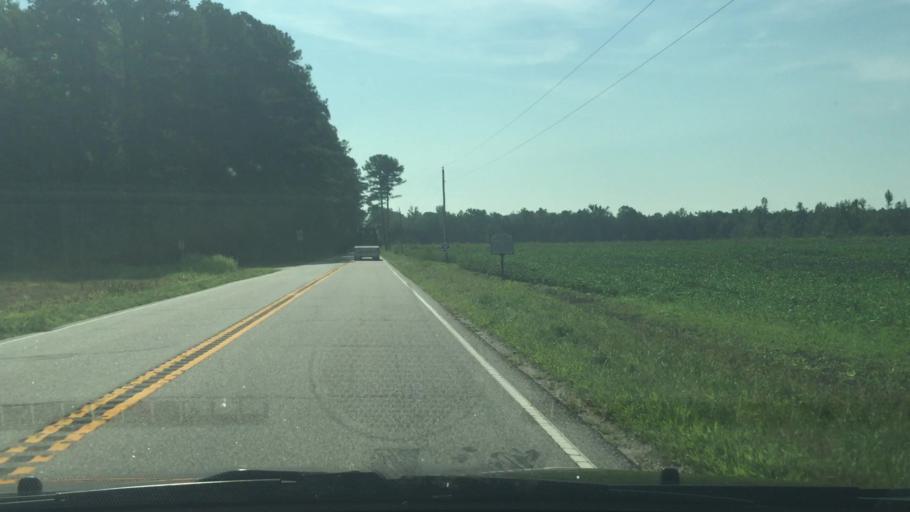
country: US
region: Virginia
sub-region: Sussex County
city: Sussex
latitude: 36.9906
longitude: -77.2551
